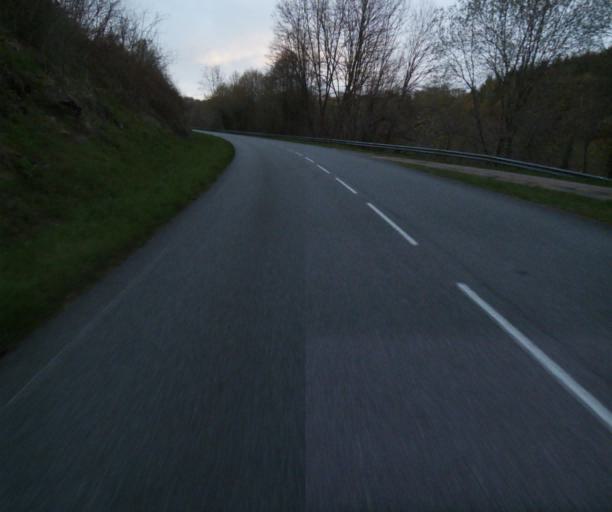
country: FR
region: Limousin
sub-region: Departement de la Correze
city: Laguenne
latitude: 45.2546
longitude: 1.8033
